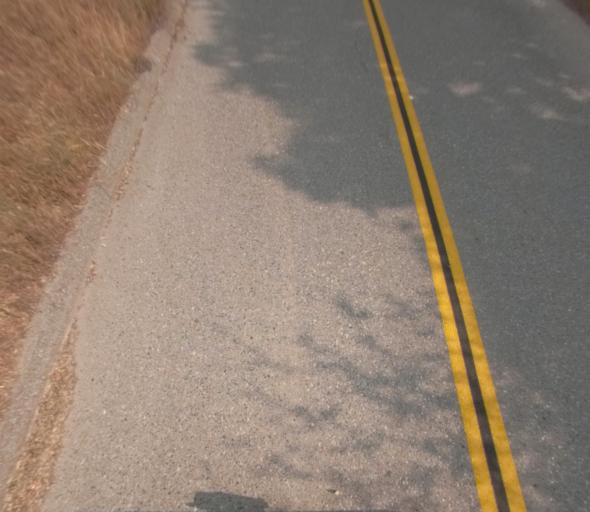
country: US
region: California
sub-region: Madera County
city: Coarsegold
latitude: 37.1985
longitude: -119.6880
